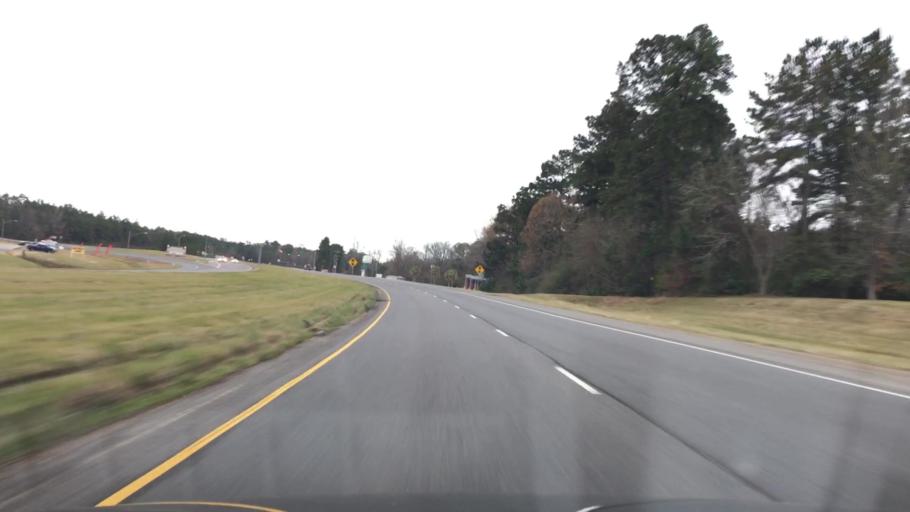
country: US
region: Louisiana
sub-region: Vernon Parish
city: New Llano
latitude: 31.0695
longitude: -93.2743
